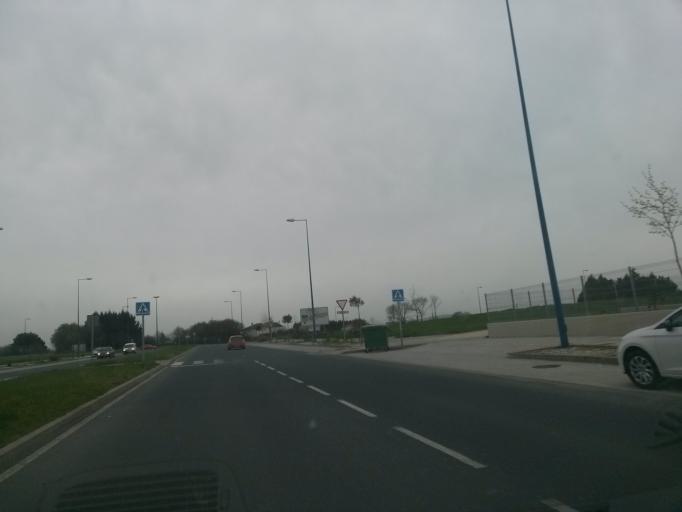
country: ES
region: Galicia
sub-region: Provincia de Lugo
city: Lugo
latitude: 43.0363
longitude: -7.5550
